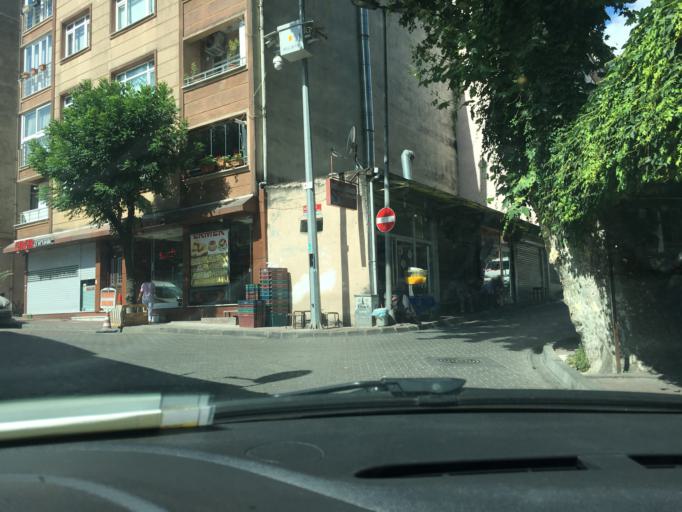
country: TR
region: Istanbul
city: Istanbul
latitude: 41.0197
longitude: 28.9550
